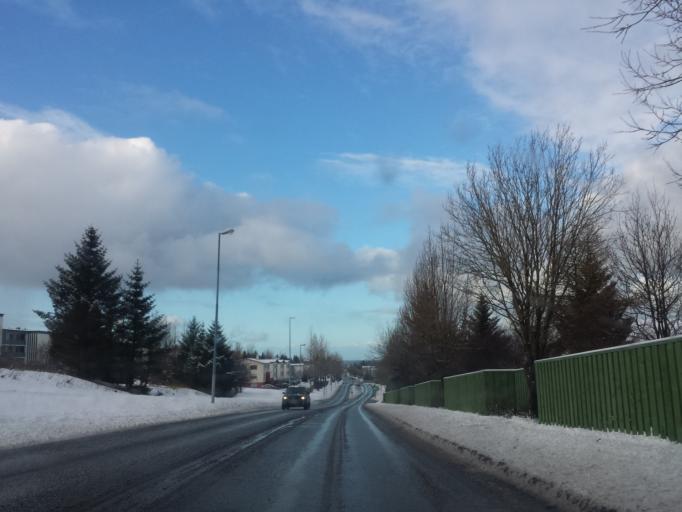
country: IS
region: Capital Region
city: Reykjavik
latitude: 64.1137
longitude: -21.8698
